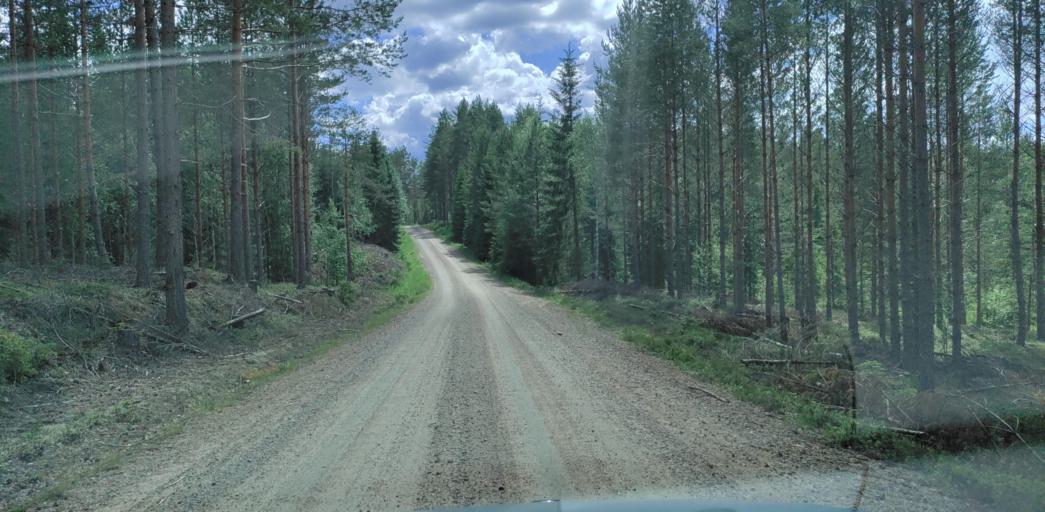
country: SE
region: Vaermland
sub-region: Hagfors Kommun
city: Ekshaerad
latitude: 60.0657
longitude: 13.2902
